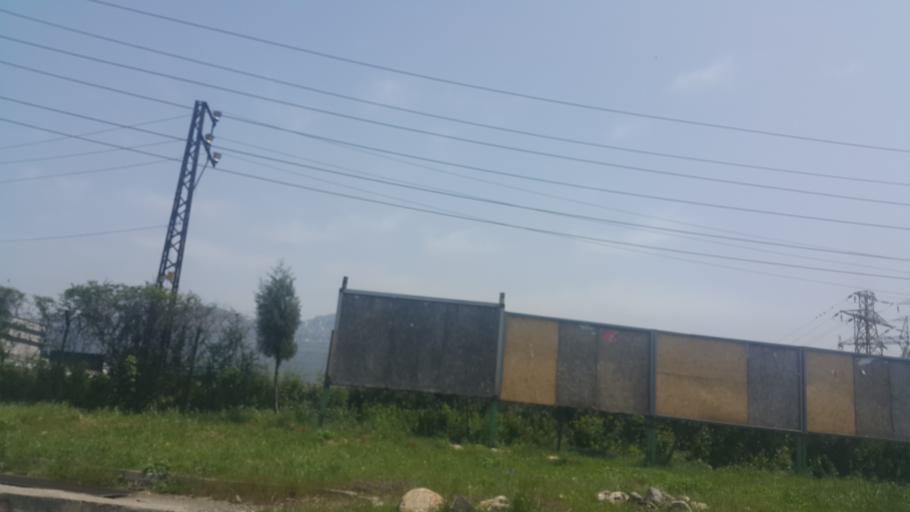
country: TR
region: Hatay
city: Yakacik
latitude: 36.7470
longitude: 36.2160
